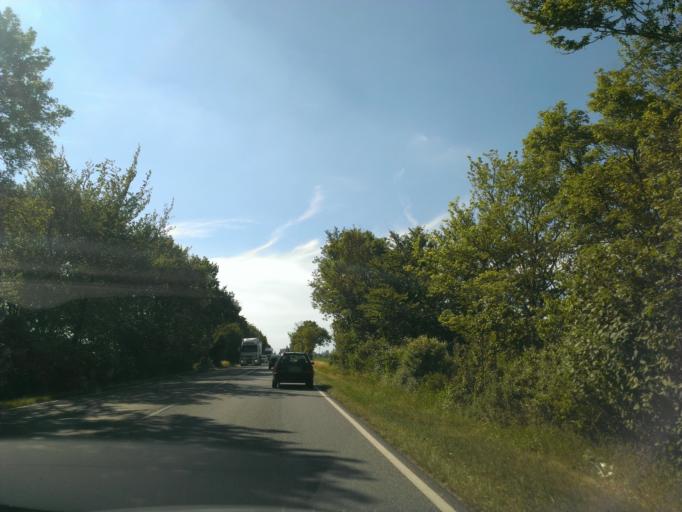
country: DE
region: Bavaria
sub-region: Swabia
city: Reimlingen
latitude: 48.8327
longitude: 10.5320
